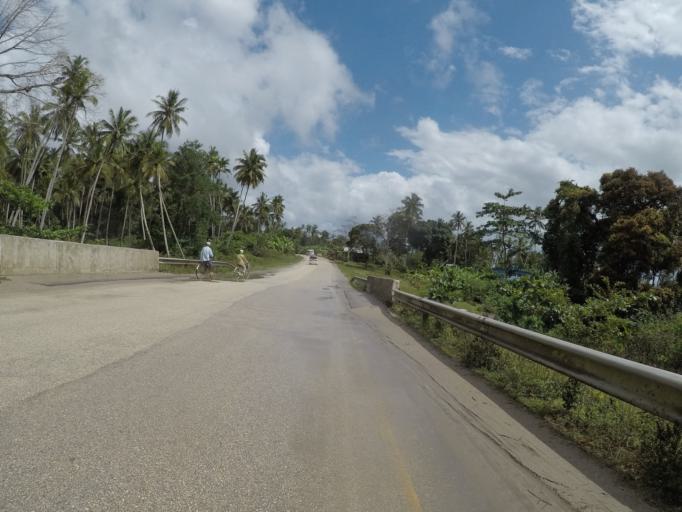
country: TZ
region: Zanzibar North
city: Gamba
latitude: -5.9789
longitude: 39.2492
